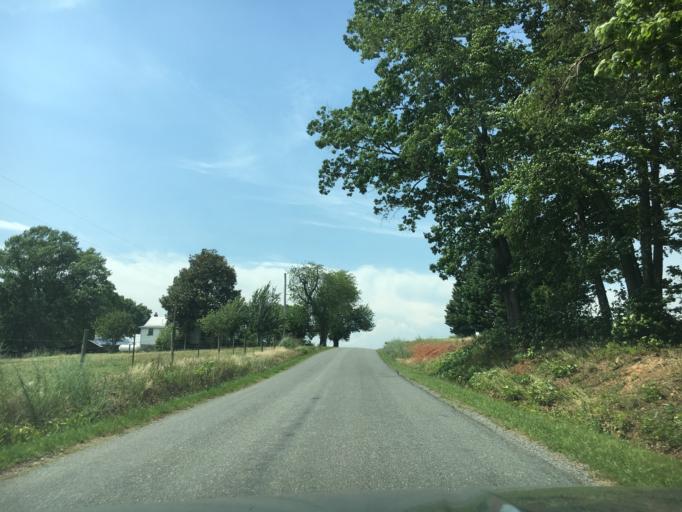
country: US
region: Virginia
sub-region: Pittsylvania County
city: Gretna
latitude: 36.9049
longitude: -79.4084
